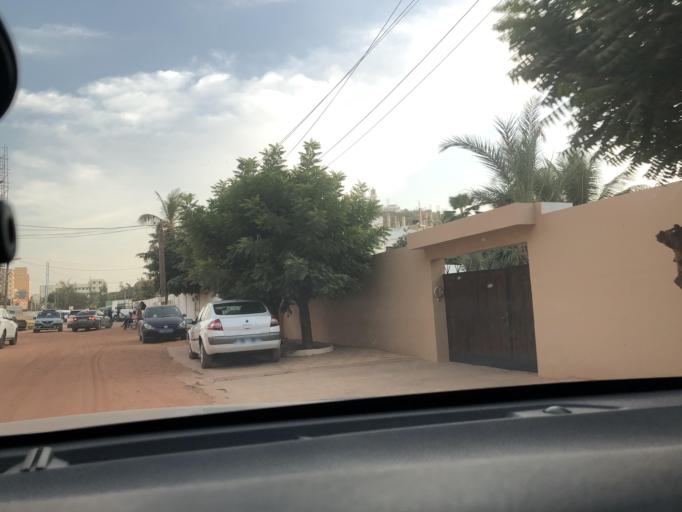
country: SN
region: Dakar
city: Mermoz Boabab
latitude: 14.7279
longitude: -17.5016
